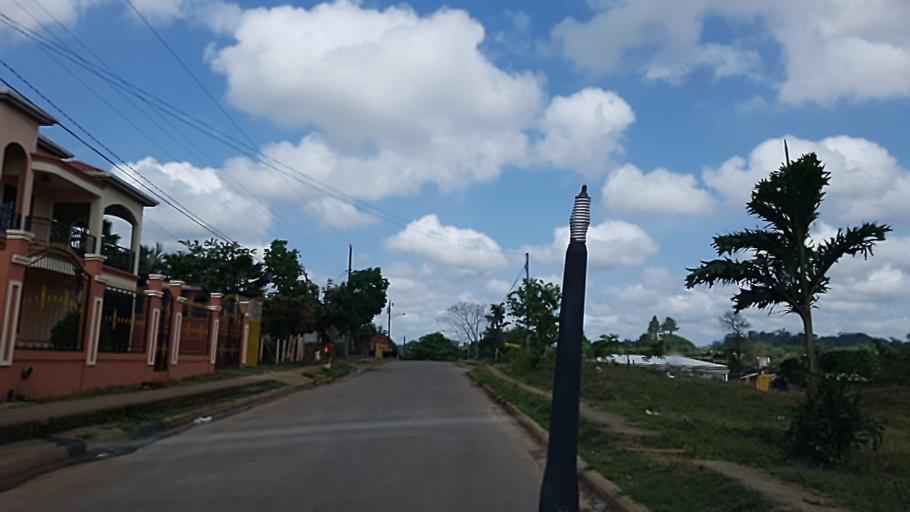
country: NI
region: Atlantico Sur
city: Nueva Guinea
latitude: 11.6862
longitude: -84.4583
